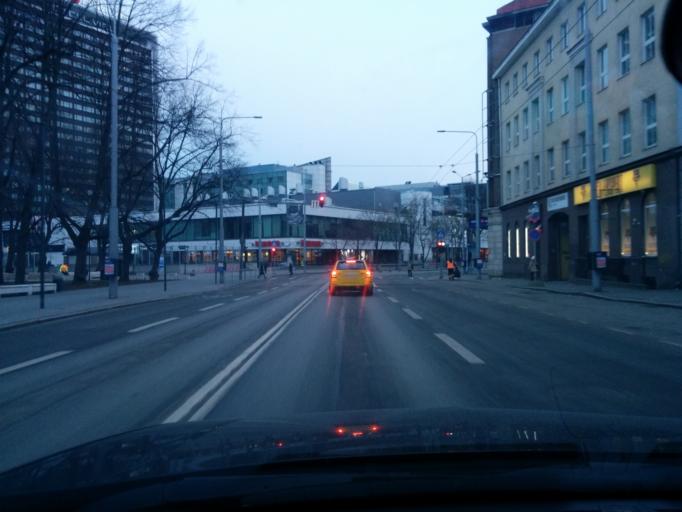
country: EE
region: Harju
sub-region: Tallinna linn
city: Tallinn
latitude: 59.4351
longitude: 24.7532
